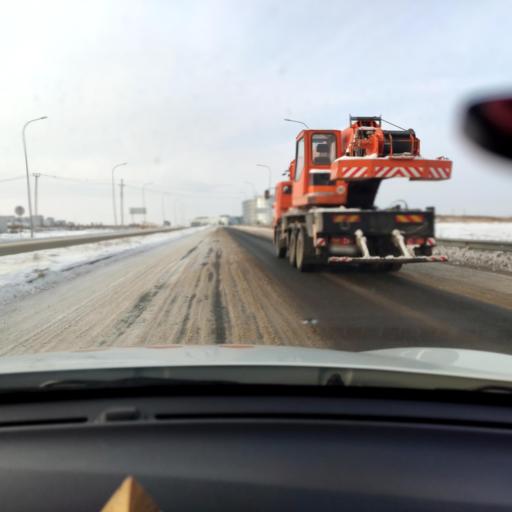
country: RU
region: Tatarstan
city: Sviyazhsk
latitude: 55.7486
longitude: 48.7602
